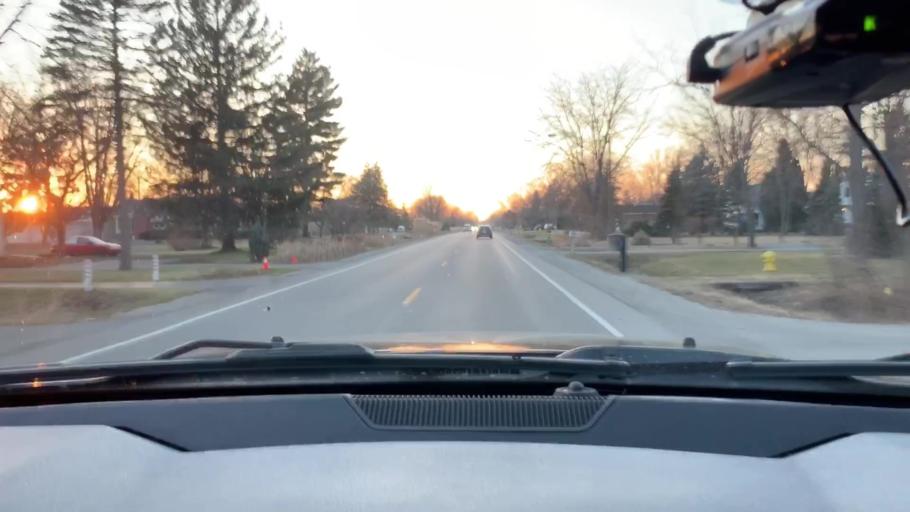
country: US
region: Michigan
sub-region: Wayne County
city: Flat Rock
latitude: 42.1237
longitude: -83.2788
